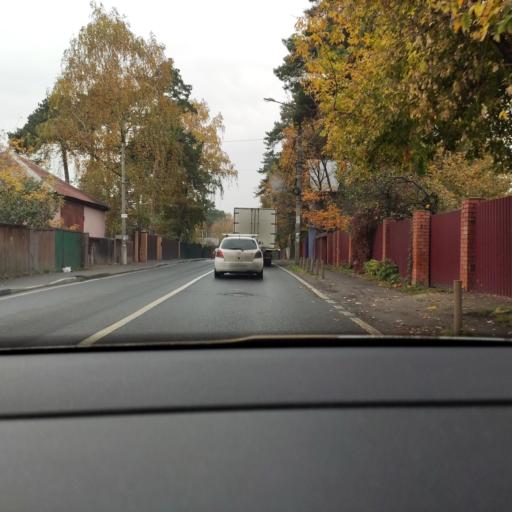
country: RU
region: Moskovskaya
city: Druzhba
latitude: 55.8854
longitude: 37.7408
